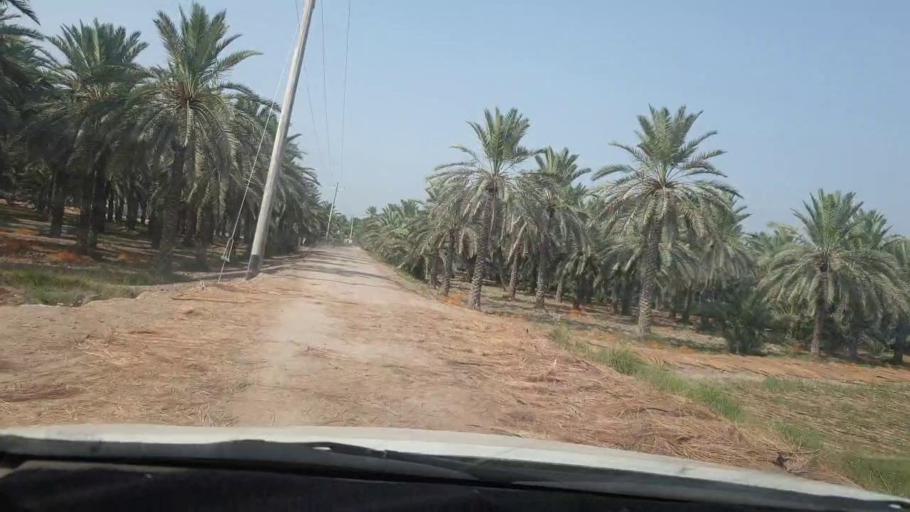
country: PK
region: Sindh
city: Rohri
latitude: 27.5947
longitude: 68.8659
